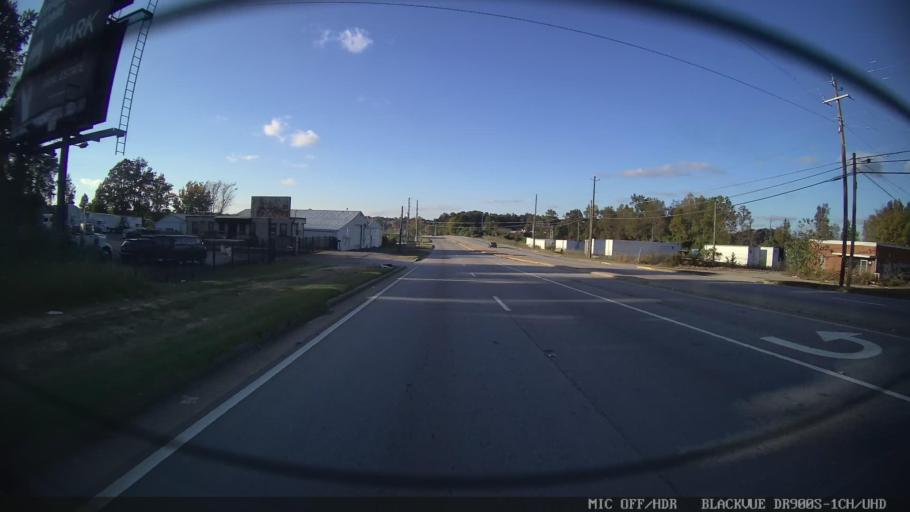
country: US
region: Georgia
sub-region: Clayton County
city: Conley
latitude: 33.6420
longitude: -84.3234
